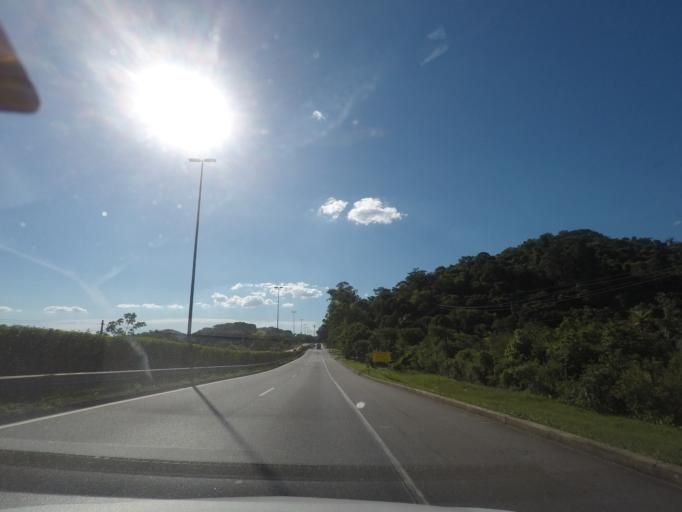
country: BR
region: Rio de Janeiro
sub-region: Sao Goncalo
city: Sao Goncalo
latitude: -22.6649
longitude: -43.1091
